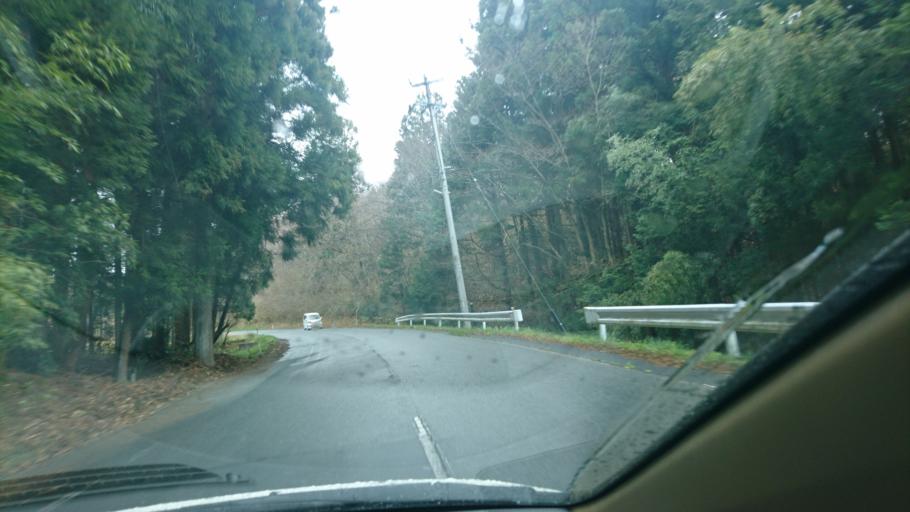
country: JP
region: Iwate
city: Ichinoseki
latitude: 38.9343
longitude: 141.3175
